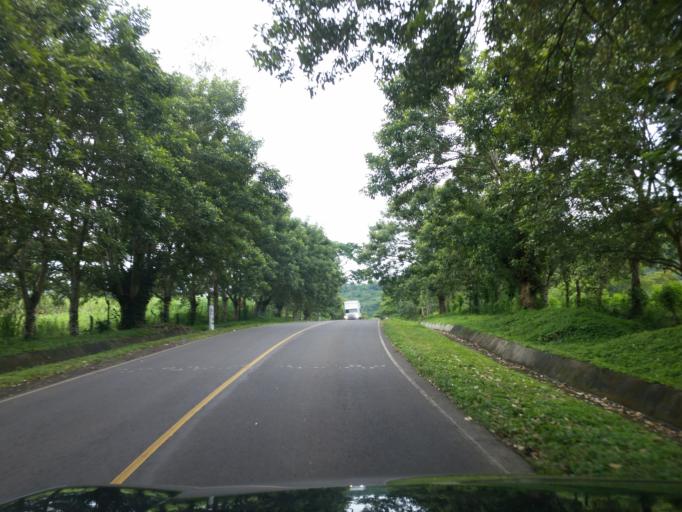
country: NI
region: Matagalpa
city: San Ramon
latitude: 13.0417
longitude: -85.7703
